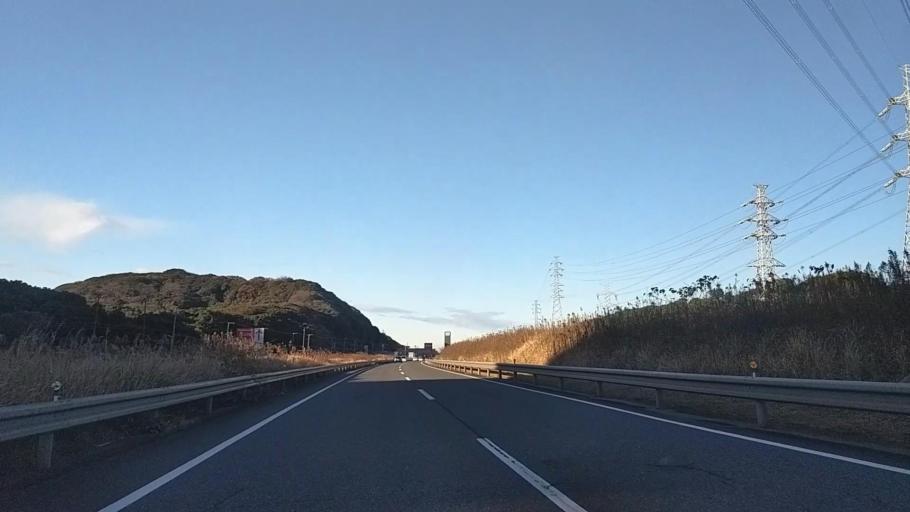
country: JP
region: Chiba
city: Kimitsu
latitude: 35.3464
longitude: 139.8865
